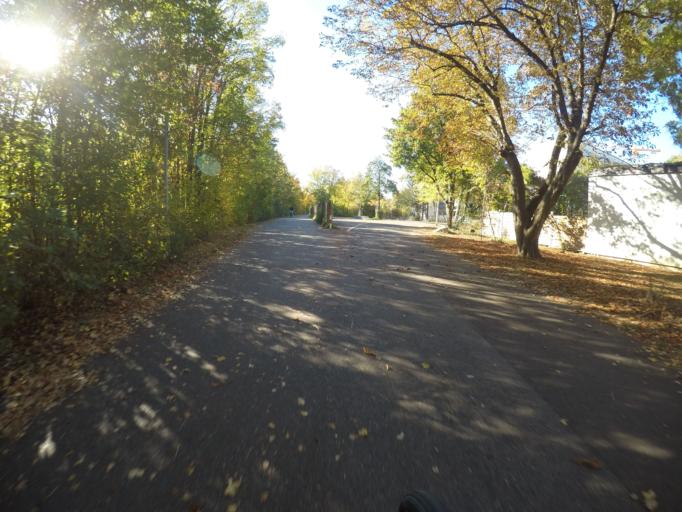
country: DE
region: Baden-Wuerttemberg
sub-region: Regierungsbezirk Stuttgart
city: Filderstadt
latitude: 48.6723
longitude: 9.2139
